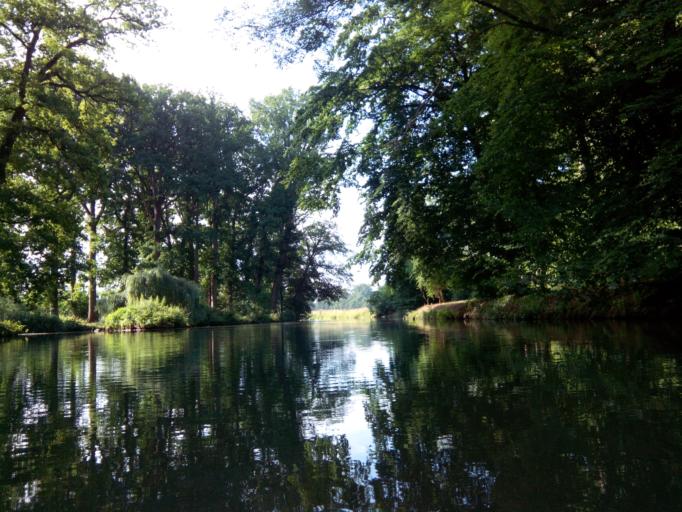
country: NL
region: Utrecht
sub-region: Gemeente Utrecht
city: Lunetten
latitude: 52.0704
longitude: 5.1559
